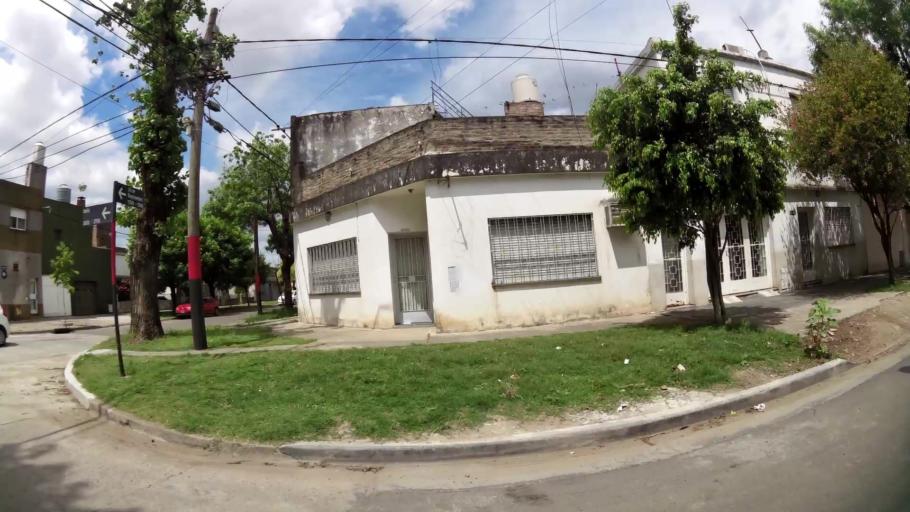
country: AR
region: Santa Fe
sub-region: Departamento de Rosario
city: Rosario
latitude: -32.9786
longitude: -60.6564
